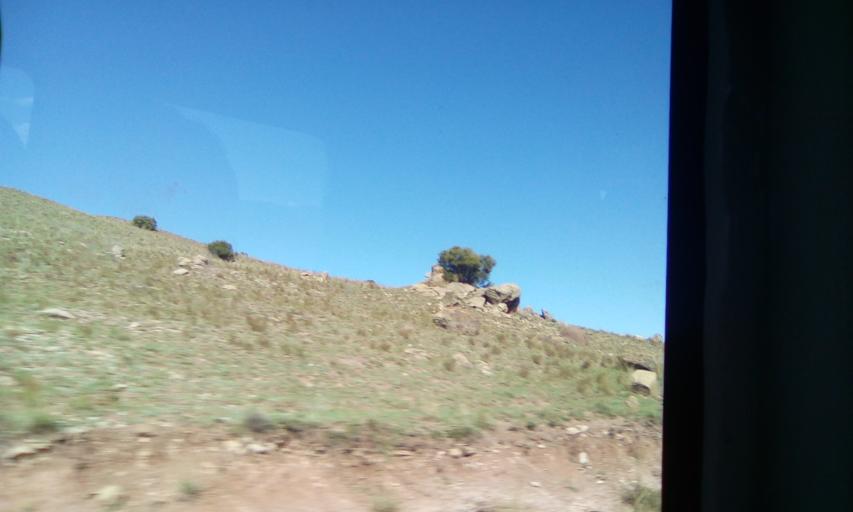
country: LS
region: Qacha's Nek
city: Qacha's Nek
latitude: -30.0387
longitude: 28.3494
